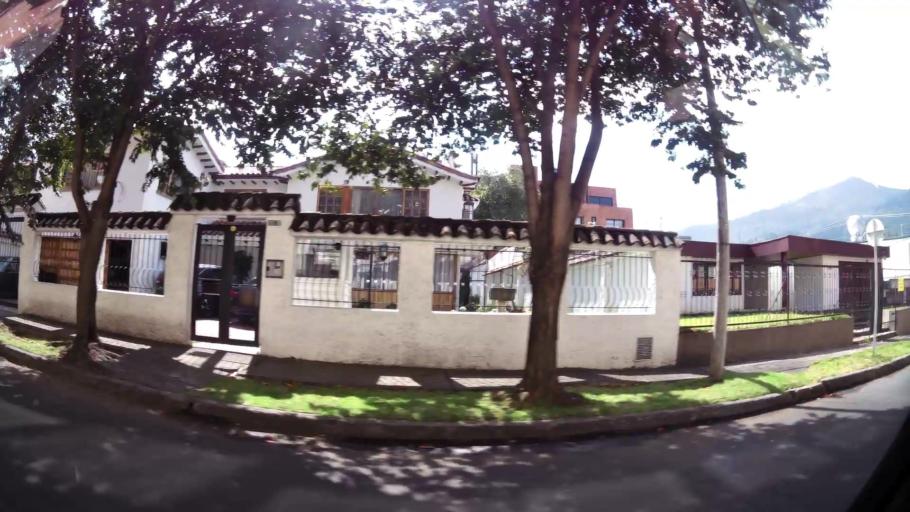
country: CO
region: Bogota D.C.
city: Barrio San Luis
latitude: 4.6909
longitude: -74.0333
